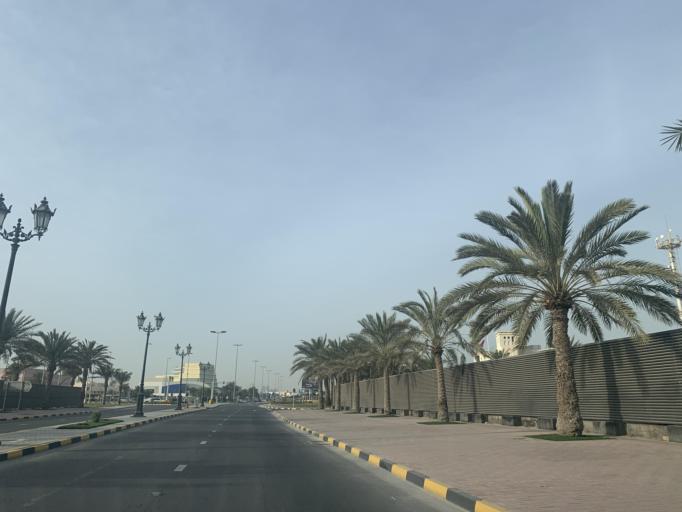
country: BH
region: Muharraq
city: Al Muharraq
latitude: 26.2703
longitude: 50.6234
